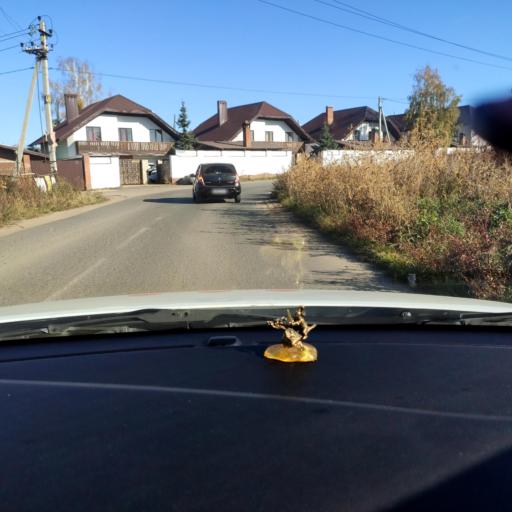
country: RU
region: Tatarstan
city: Vysokaya Gora
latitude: 55.8340
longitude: 49.2310
